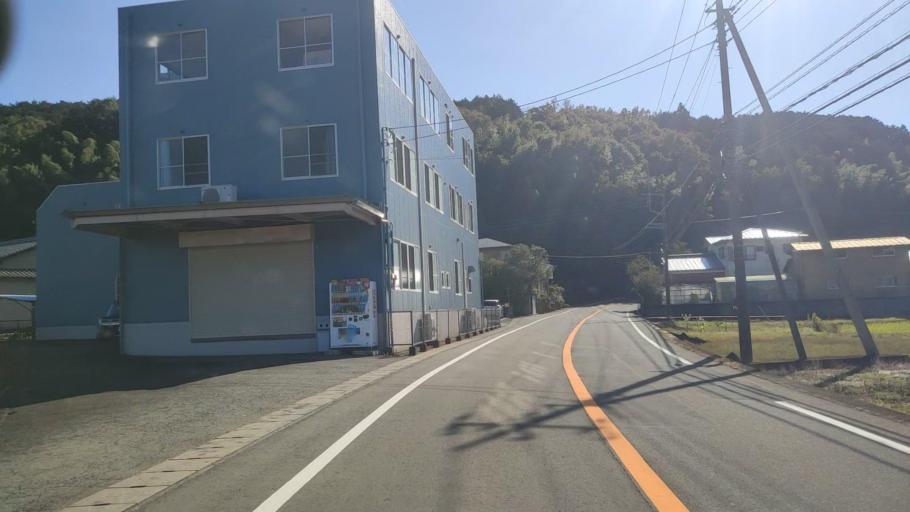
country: JP
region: Shizuoka
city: Atami
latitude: 35.0274
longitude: 139.0120
